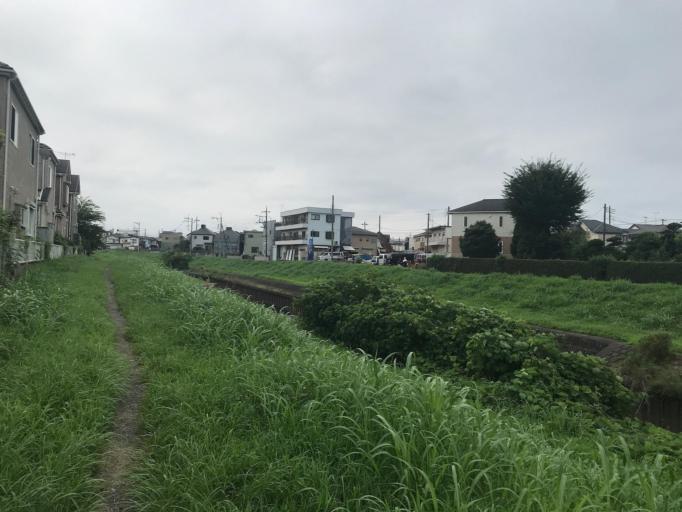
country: JP
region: Saitama
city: Asaka
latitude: 35.7889
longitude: 139.5788
